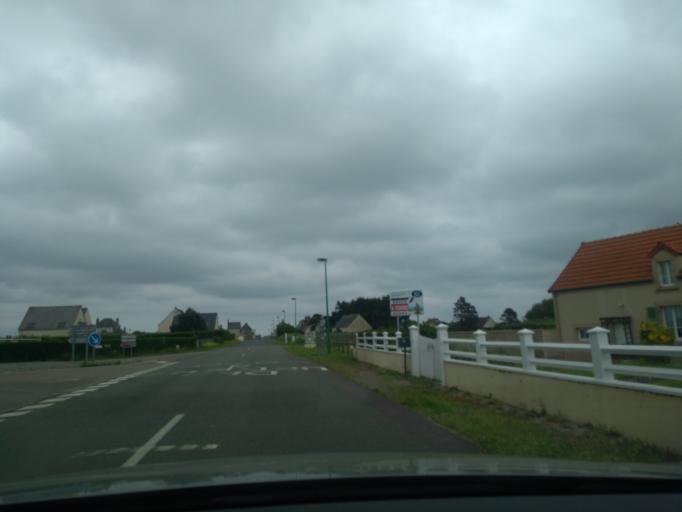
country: FR
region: Lower Normandy
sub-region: Departement de la Manche
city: Sainte-Mere-Eglise
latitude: 49.4708
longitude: -1.2492
